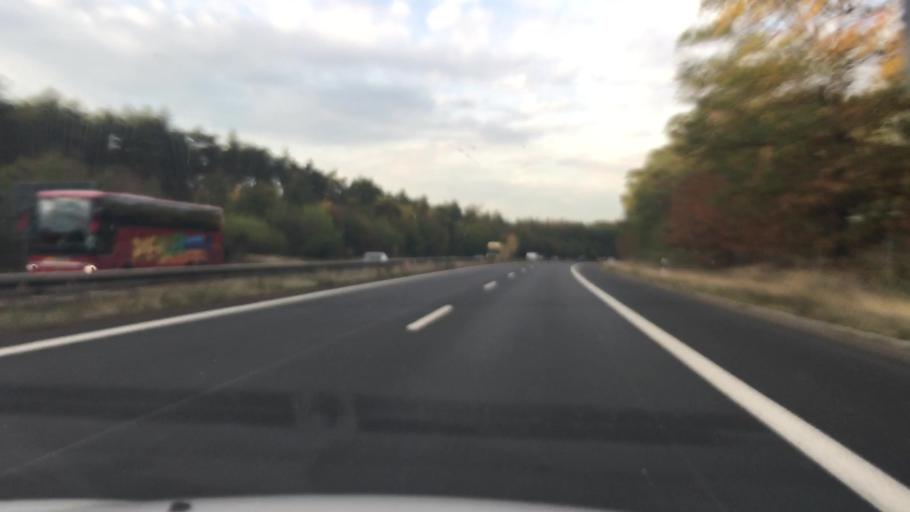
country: DE
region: Saxony
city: Thiendorf
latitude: 51.2730
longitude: 13.7252
